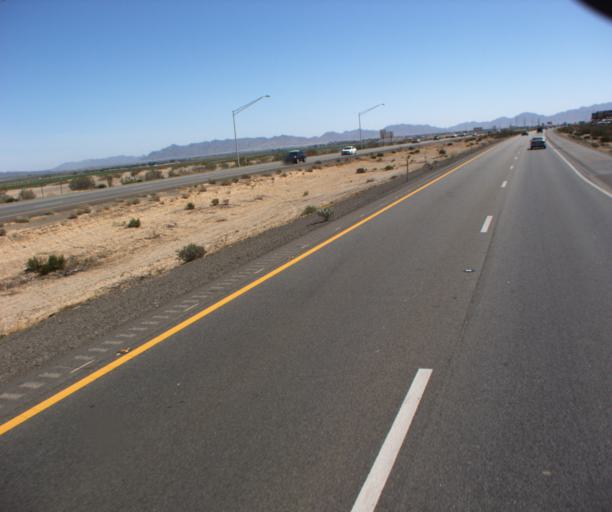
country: US
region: Arizona
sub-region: Yuma County
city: Yuma
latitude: 32.6874
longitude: -114.5738
